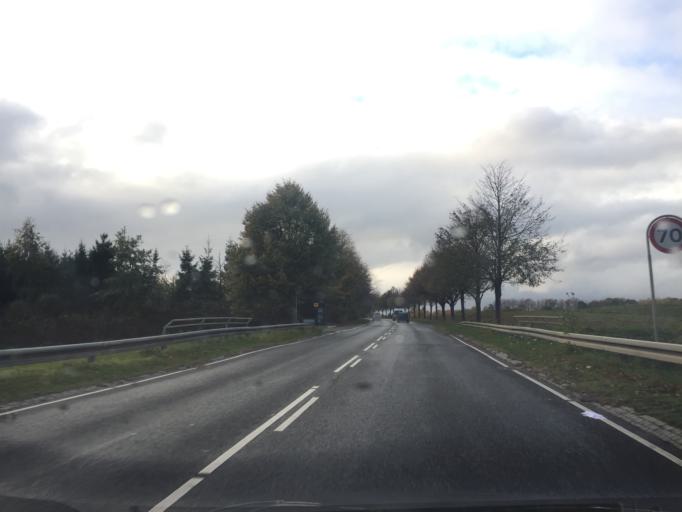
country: DK
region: Capital Region
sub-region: Fredensborg Kommune
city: Humlebaek
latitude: 55.9665
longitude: 12.5124
